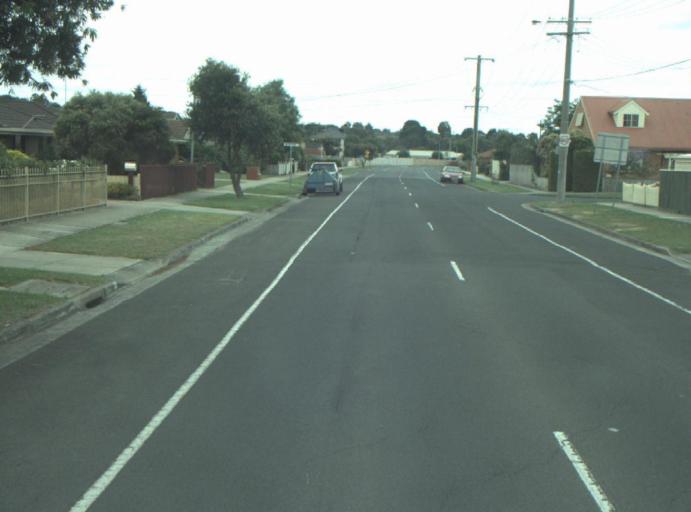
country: AU
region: Victoria
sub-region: Greater Geelong
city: Wandana Heights
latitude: -38.1993
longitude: 144.3271
